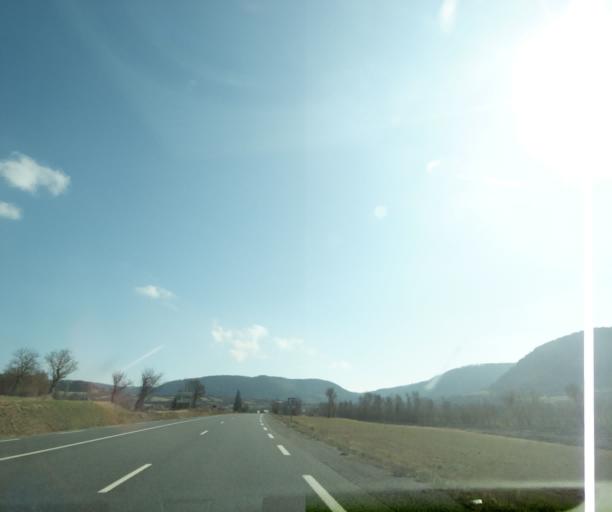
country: FR
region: Languedoc-Roussillon
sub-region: Departement de la Lozere
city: Chanac
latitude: 44.4798
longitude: 3.3231
